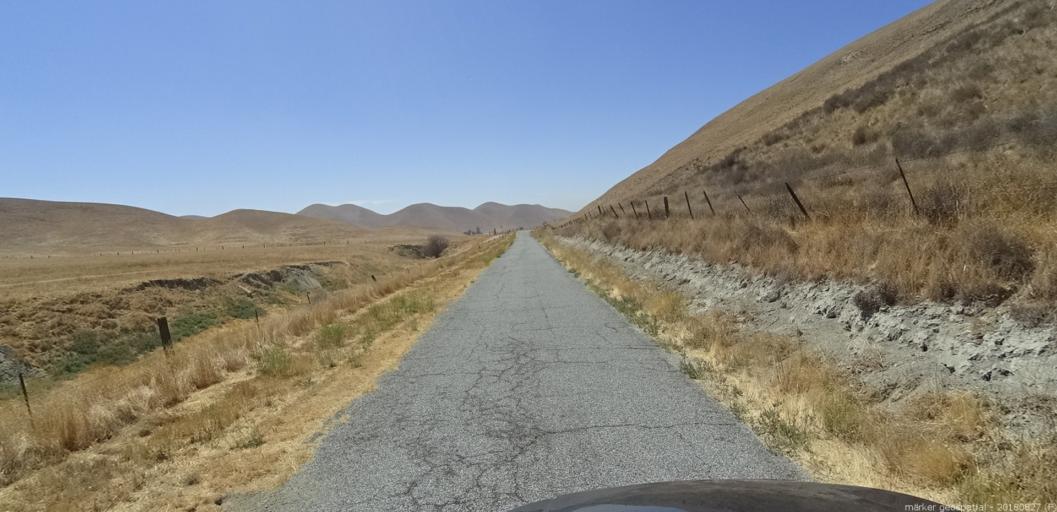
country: US
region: California
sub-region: Monterey County
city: King City
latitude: 36.1118
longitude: -120.8754
